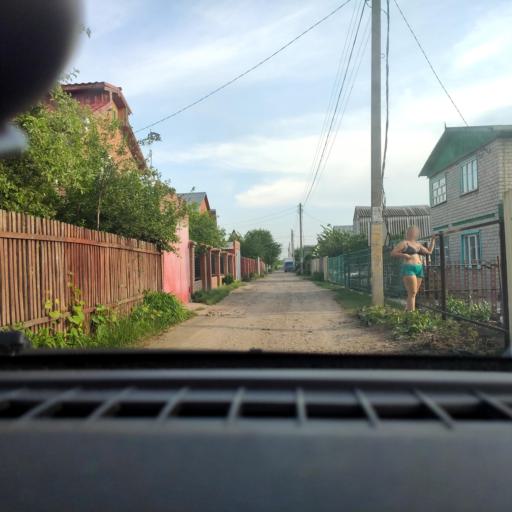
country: RU
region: Samara
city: Tol'yatti
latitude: 53.5910
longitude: 49.3234
